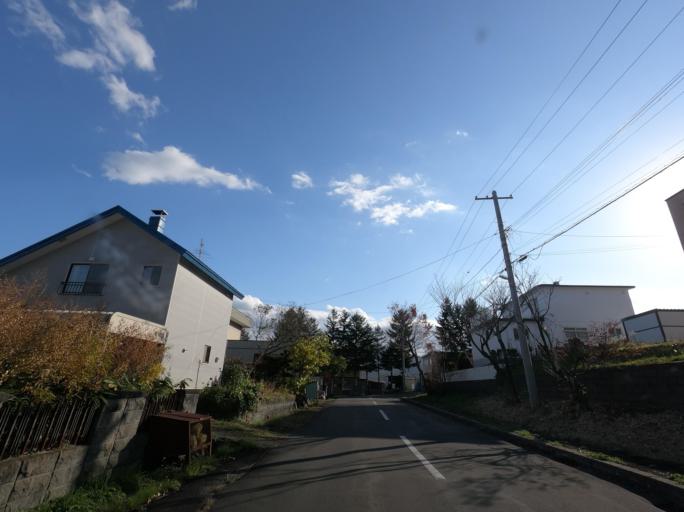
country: JP
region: Hokkaido
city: Iwamizawa
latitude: 42.9859
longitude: 142.0007
